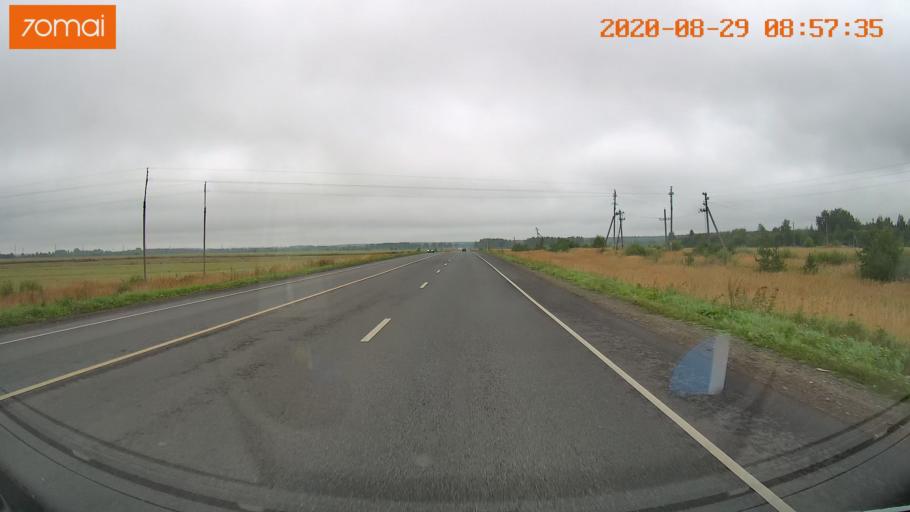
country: RU
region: Ivanovo
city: Staraya Vichuga
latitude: 57.2662
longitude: 41.9052
